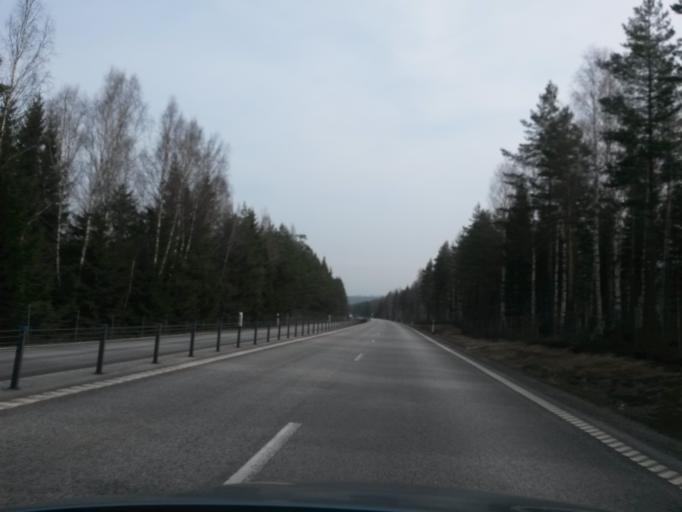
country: SE
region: Vaestra Goetaland
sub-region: Gullspangs Kommun
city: Anderstorp
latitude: 58.9208
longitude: 14.4022
